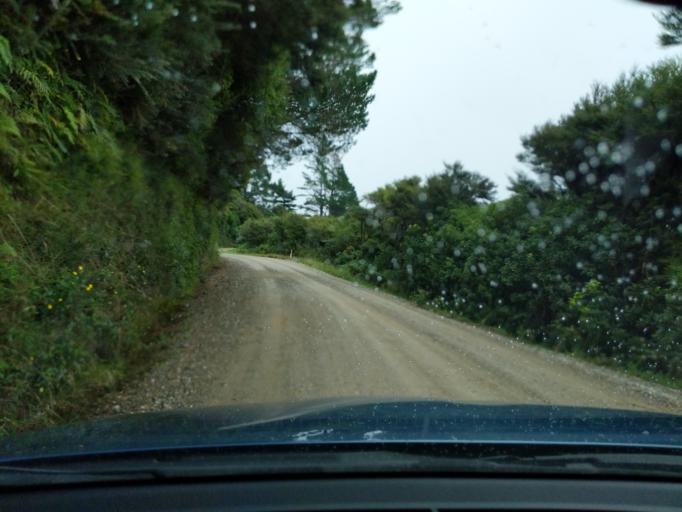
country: NZ
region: Tasman
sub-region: Tasman District
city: Takaka
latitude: -40.6301
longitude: 172.5117
